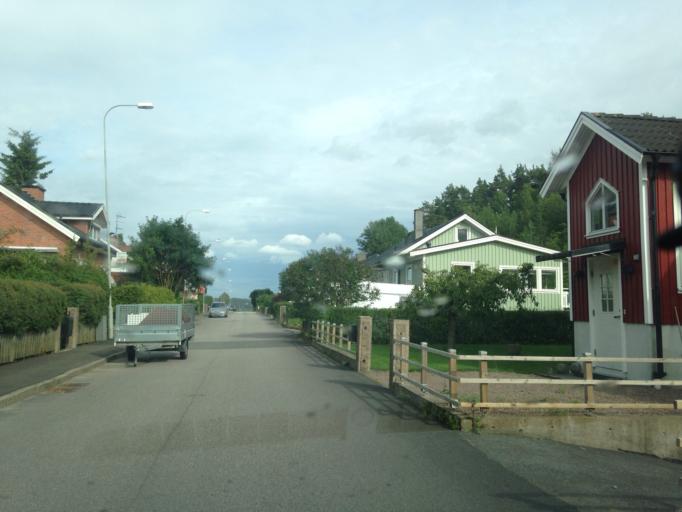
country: SE
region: Vaestra Goetaland
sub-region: Goteborg
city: Goeteborg
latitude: 57.7512
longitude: 11.9693
